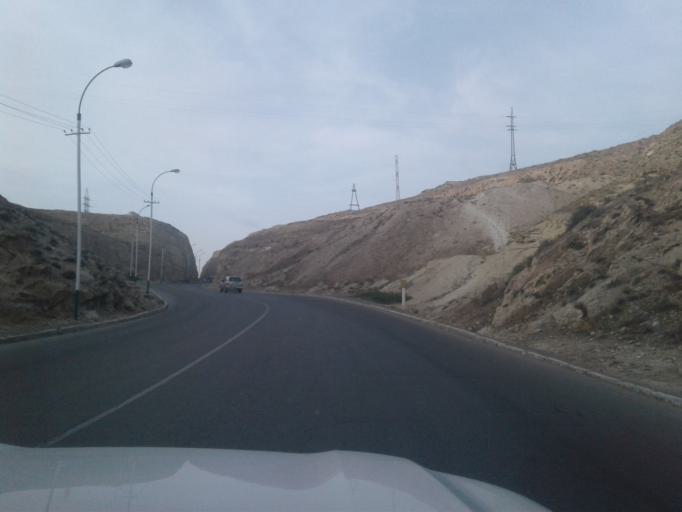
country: TM
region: Balkan
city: Turkmenbasy
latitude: 40.0354
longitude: 52.9688
